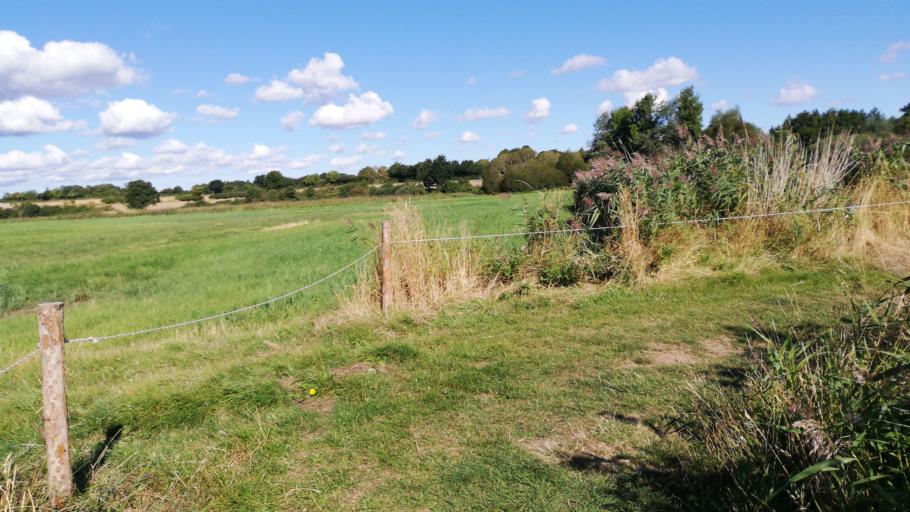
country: DE
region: Schleswig-Holstein
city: Steinberg
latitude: 54.7954
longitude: 9.7664
